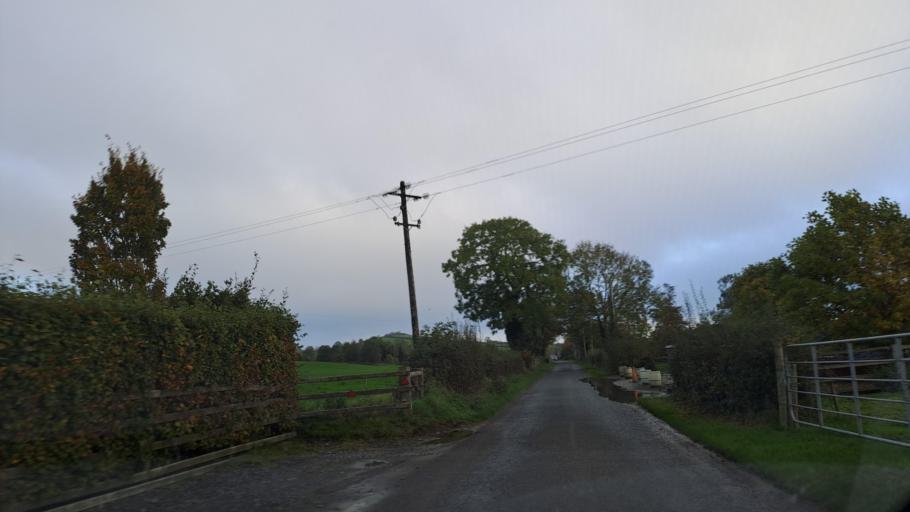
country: IE
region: Ulster
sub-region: County Monaghan
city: Carrickmacross
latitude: 53.9759
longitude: -6.6713
